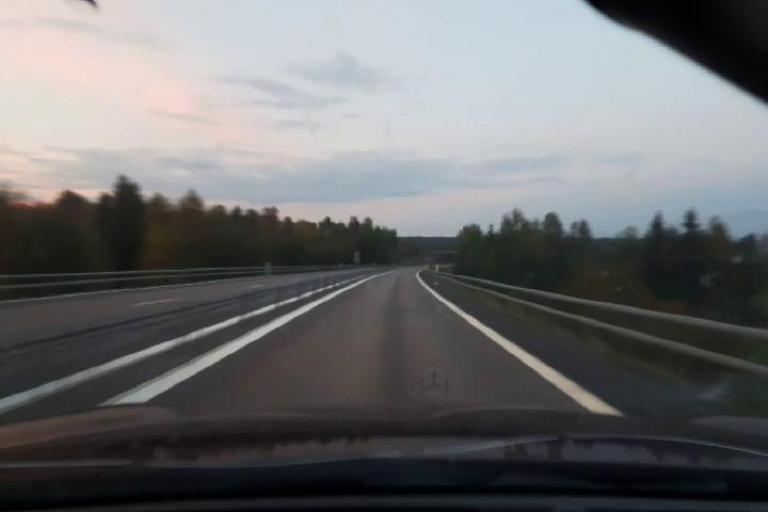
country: SE
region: Vaesternorrland
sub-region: Haernoesands Kommun
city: Haernoesand
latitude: 62.8731
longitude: 18.0480
